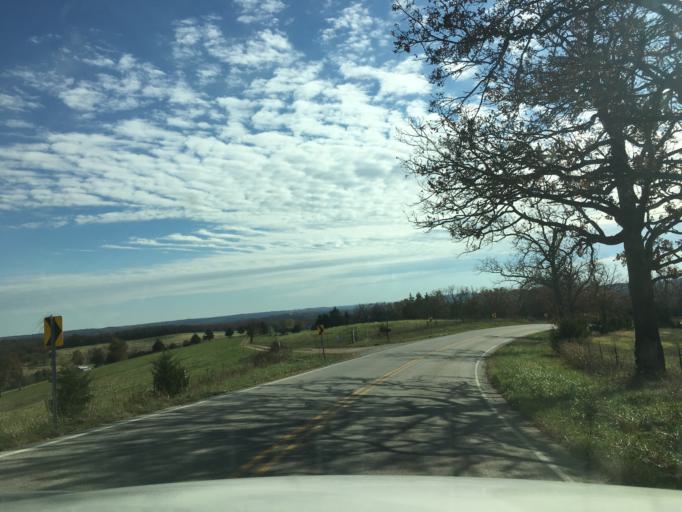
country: US
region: Missouri
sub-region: Osage County
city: Linn
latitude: 38.4122
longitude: -91.8150
